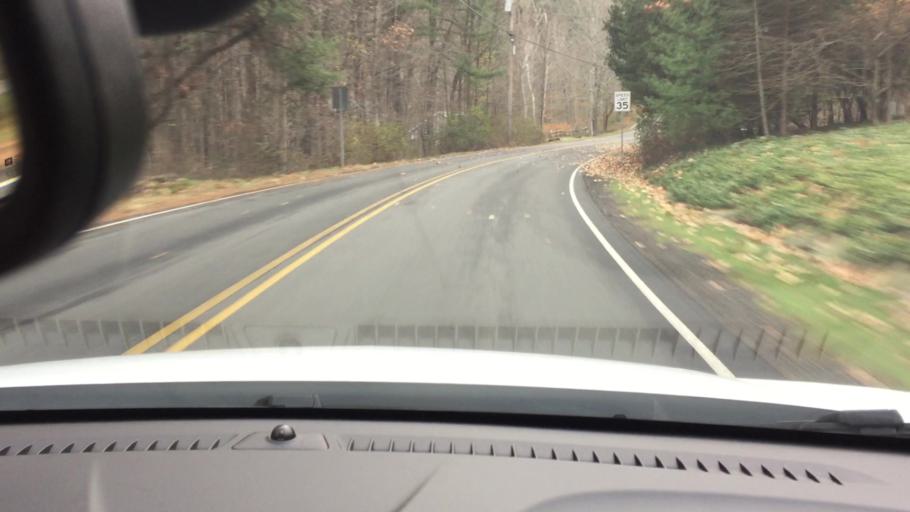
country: US
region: Massachusetts
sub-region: Berkshire County
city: New Marlborough
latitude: 42.1742
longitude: -73.1899
